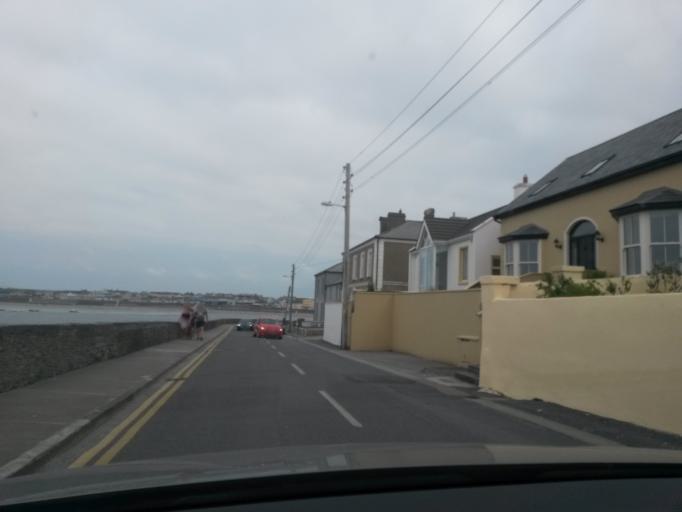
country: IE
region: Munster
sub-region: Ciarrai
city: Ballybunnion
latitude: 52.6811
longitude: -9.6568
